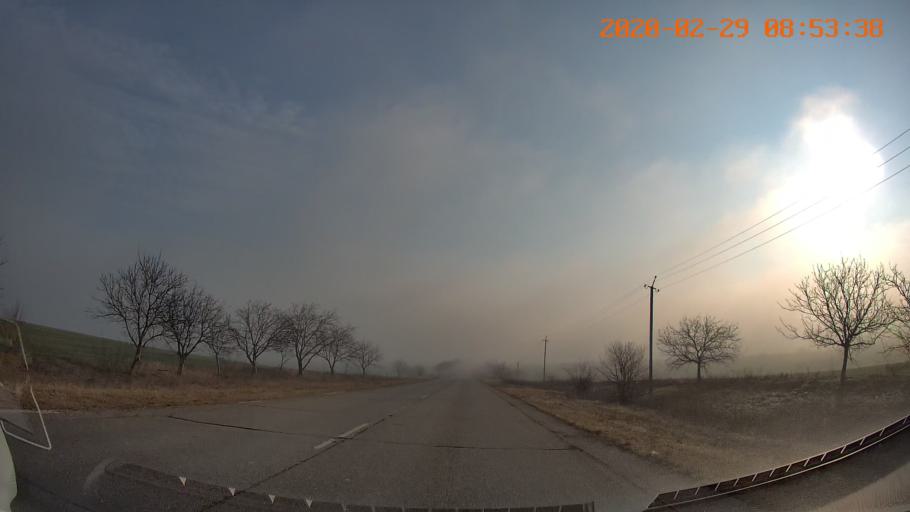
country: MD
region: Telenesti
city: Tiraspolul Nou
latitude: 46.9262
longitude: 29.5605
